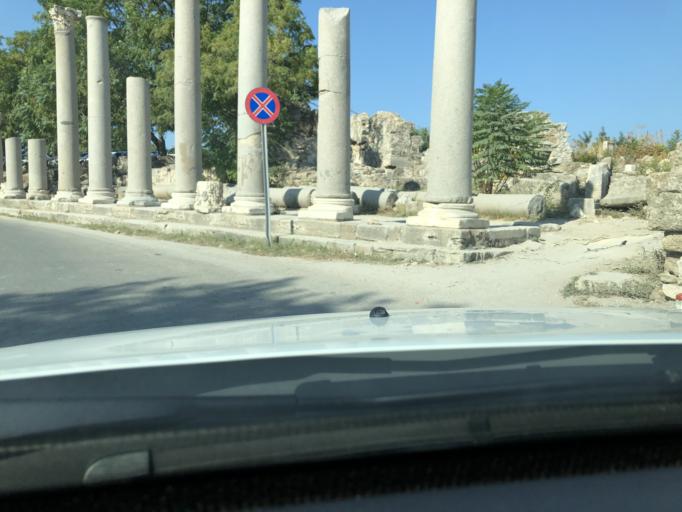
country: TR
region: Antalya
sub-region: Manavgat
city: Side
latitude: 36.7688
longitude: 31.3902
